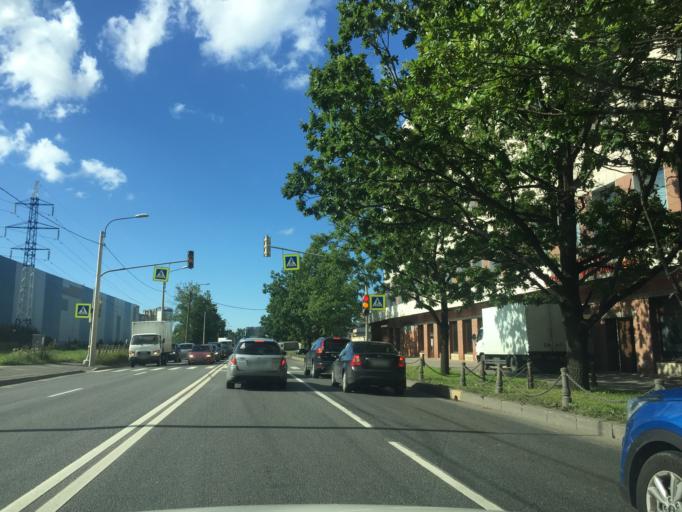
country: RU
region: St.-Petersburg
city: Dachnoye
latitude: 59.8417
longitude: 30.2983
